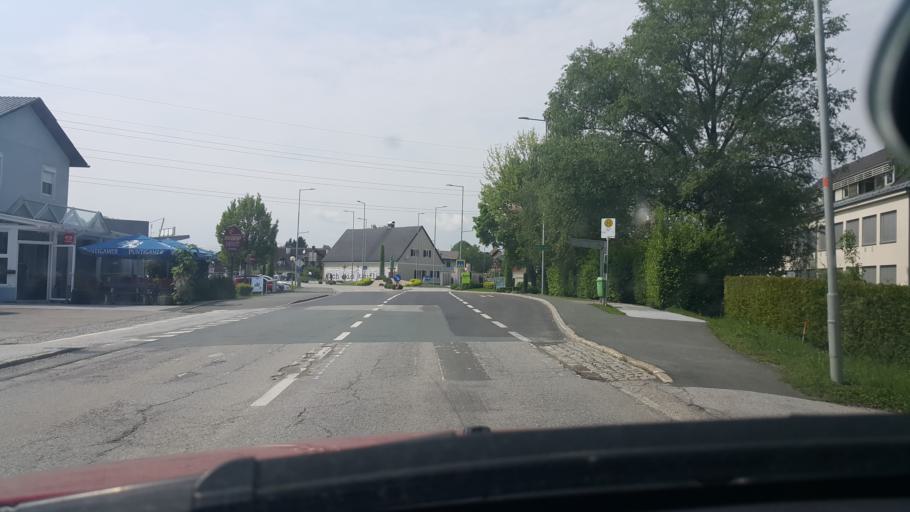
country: AT
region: Styria
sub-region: Politischer Bezirk Graz-Umgebung
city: Lieboch
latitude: 46.9737
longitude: 15.3367
